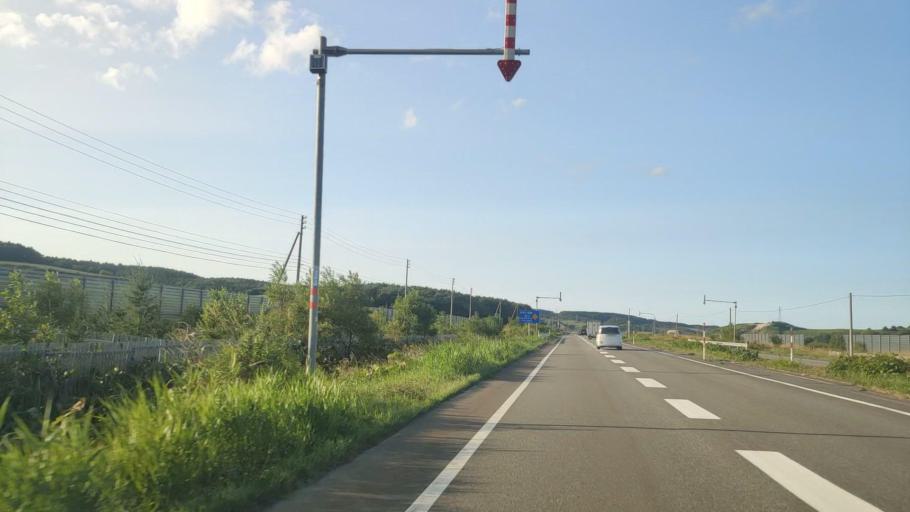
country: JP
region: Hokkaido
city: Wakkanai
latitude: 45.3215
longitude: 141.7193
